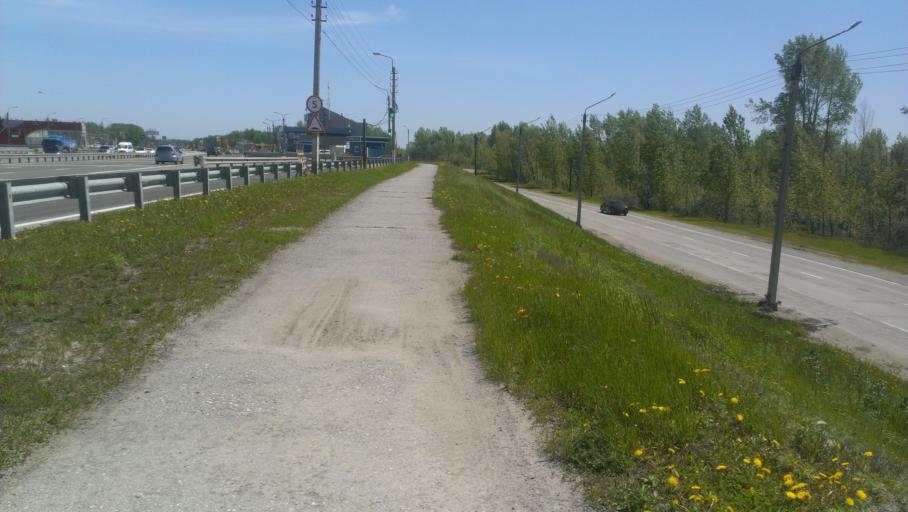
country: RU
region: Altai Krai
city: Zaton
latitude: 53.3154
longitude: 83.8282
